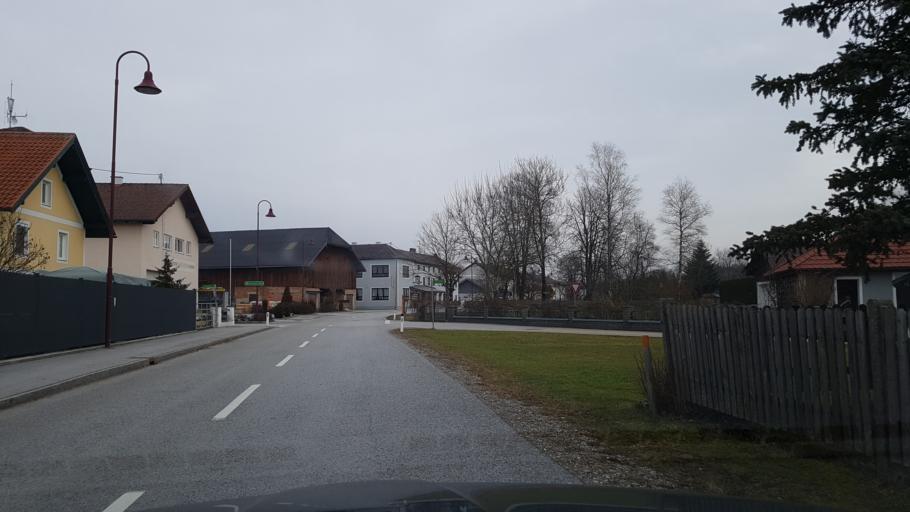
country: AT
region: Salzburg
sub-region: Politischer Bezirk Salzburg-Umgebung
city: Lamprechtshausen
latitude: 48.0434
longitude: 12.9477
